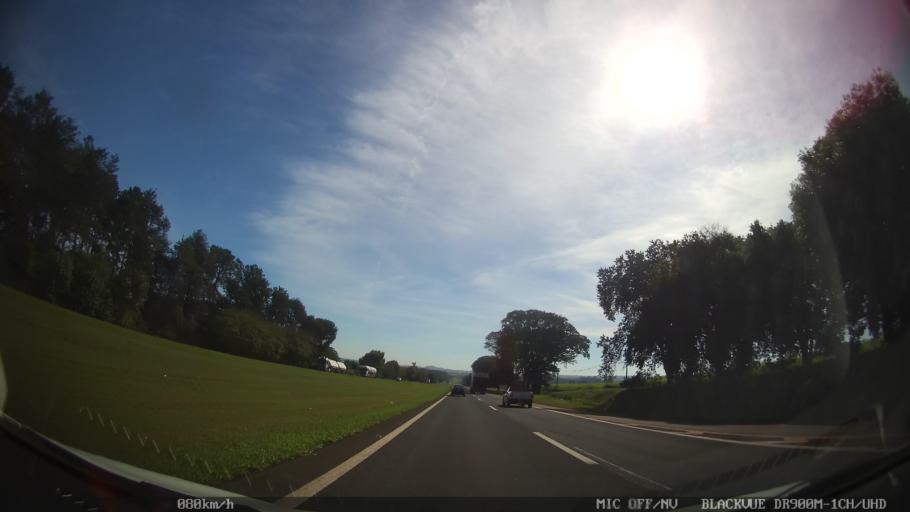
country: BR
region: Sao Paulo
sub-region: Leme
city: Leme
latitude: -22.2443
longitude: -47.3903
